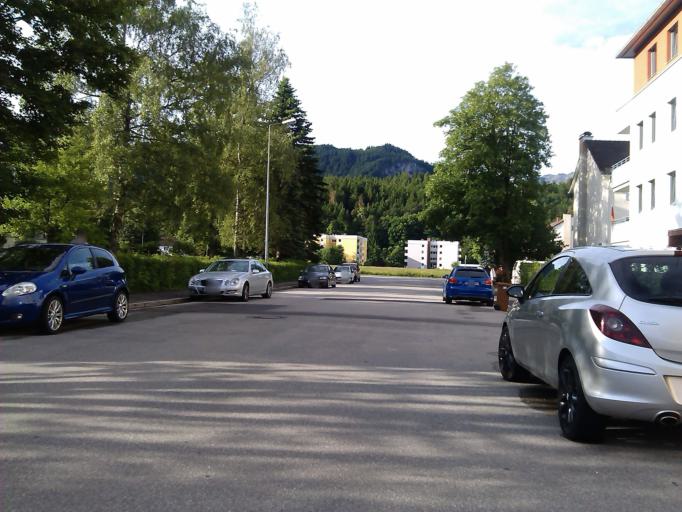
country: DE
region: Bavaria
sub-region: Swabia
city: Fuessen
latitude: 47.5712
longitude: 10.6856
